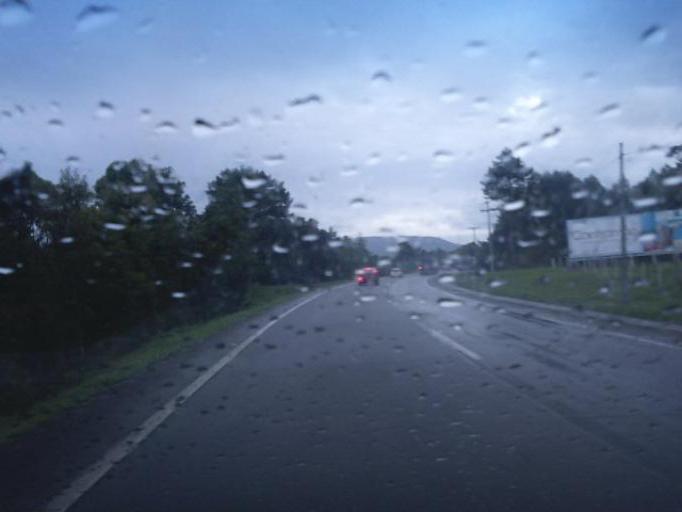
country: BR
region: Parana
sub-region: Sao Jose Dos Pinhais
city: Sao Jose dos Pinhais
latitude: -25.8446
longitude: -49.0362
